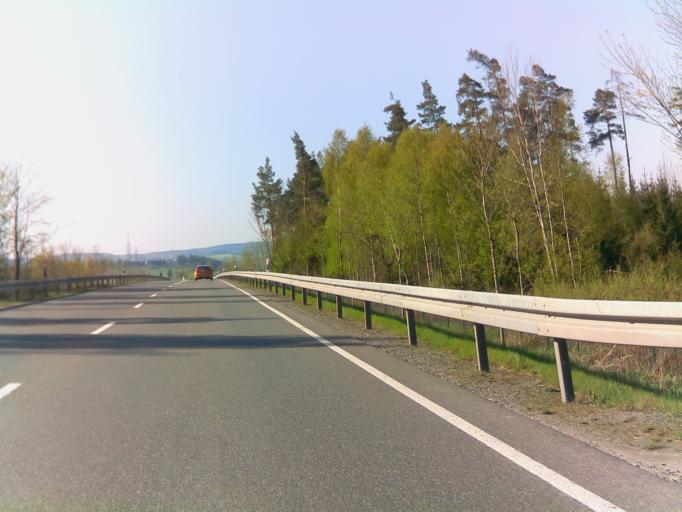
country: DE
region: Thuringia
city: Pormitz
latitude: 50.6301
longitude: 11.8144
